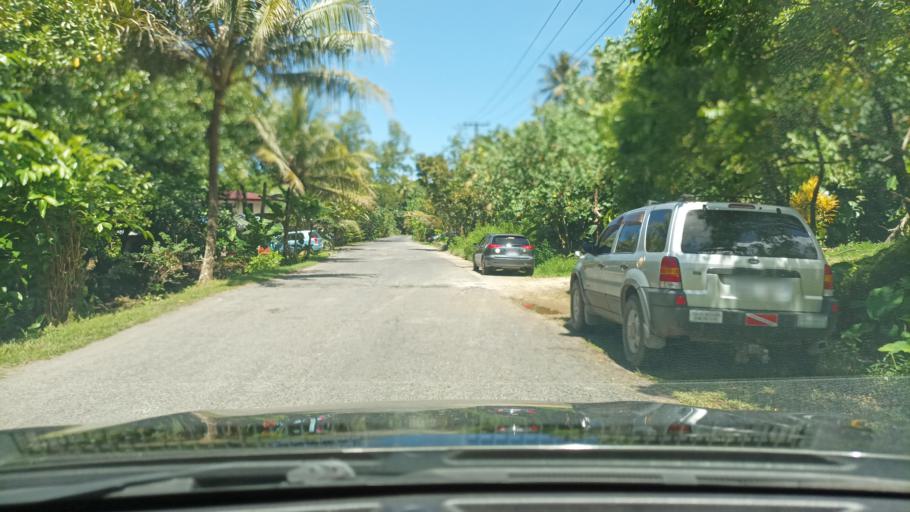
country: FM
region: Pohnpei
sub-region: Kolonia Municipality
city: Kolonia
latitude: 6.9409
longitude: 158.2762
